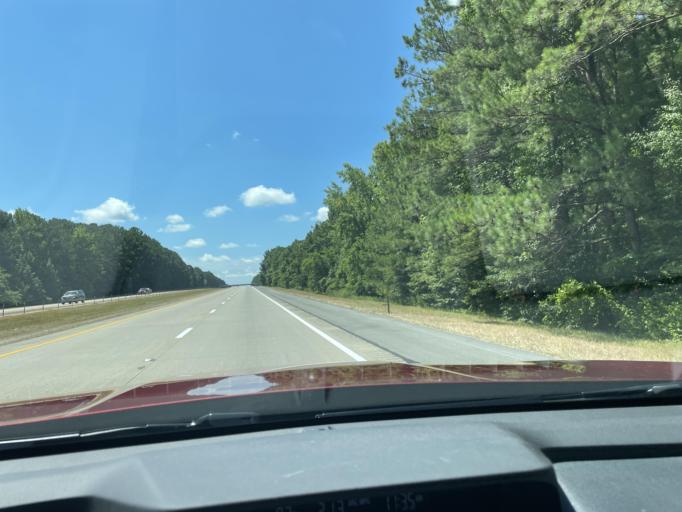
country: US
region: Arkansas
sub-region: Jefferson County
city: Redfield
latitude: 34.4471
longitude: -92.1995
